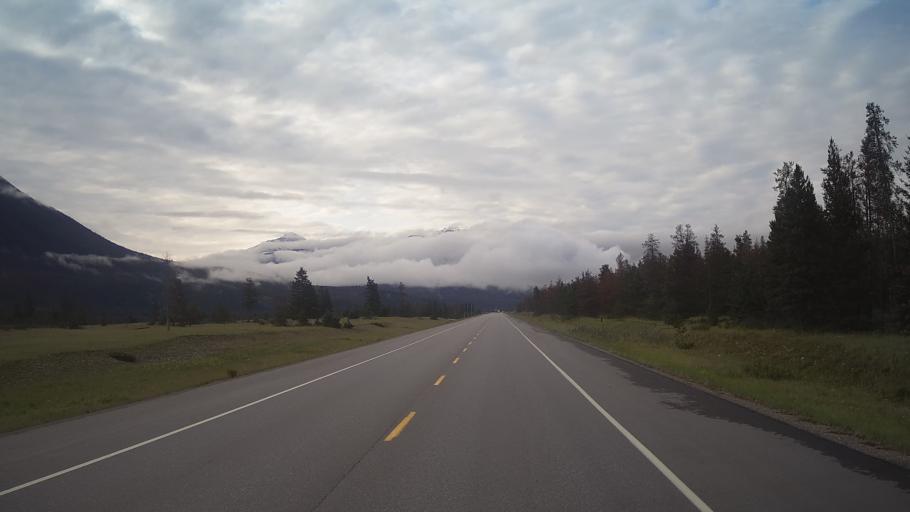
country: CA
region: Alberta
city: Jasper Park Lodge
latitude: 52.9580
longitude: -118.0472
